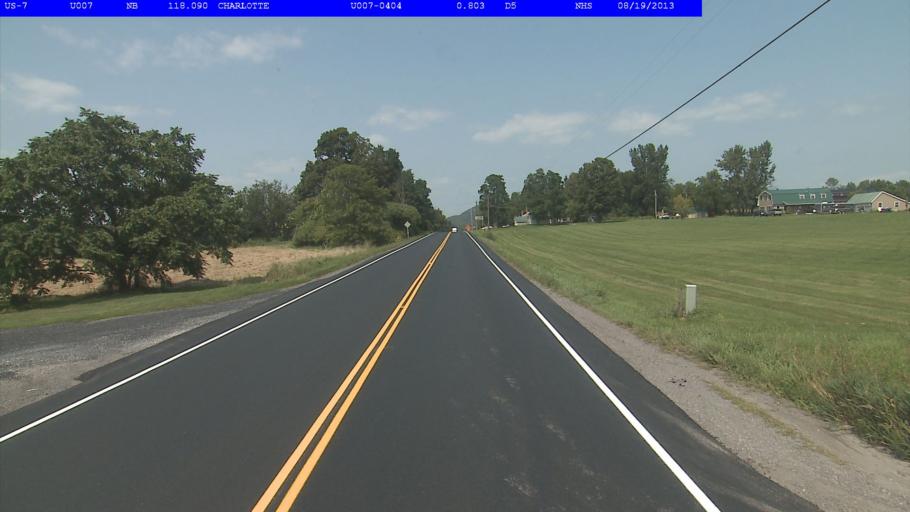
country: US
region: Vermont
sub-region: Addison County
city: Vergennes
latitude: 44.2738
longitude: -73.2341
